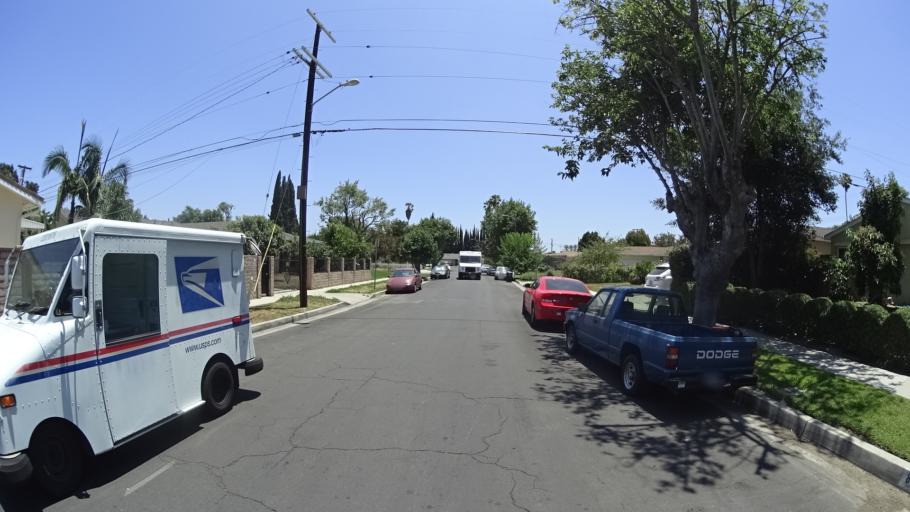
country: US
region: California
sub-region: Los Angeles County
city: Van Nuys
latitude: 34.2237
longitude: -118.4592
